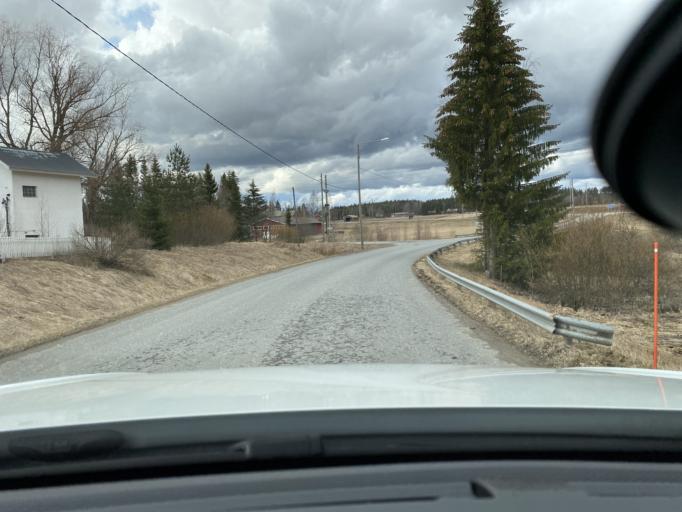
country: FI
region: Pirkanmaa
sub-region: Lounais-Pirkanmaa
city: Punkalaidun
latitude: 61.1199
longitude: 23.0514
